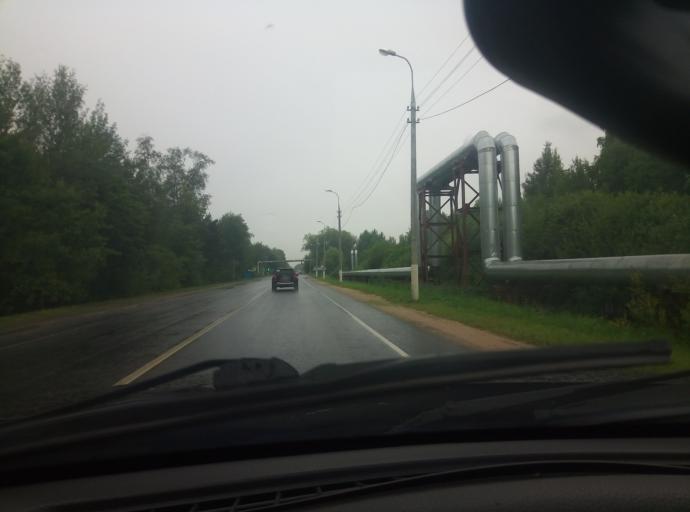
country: RU
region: Moskovskaya
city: Protvino
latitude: 54.8829
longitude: 37.2151
